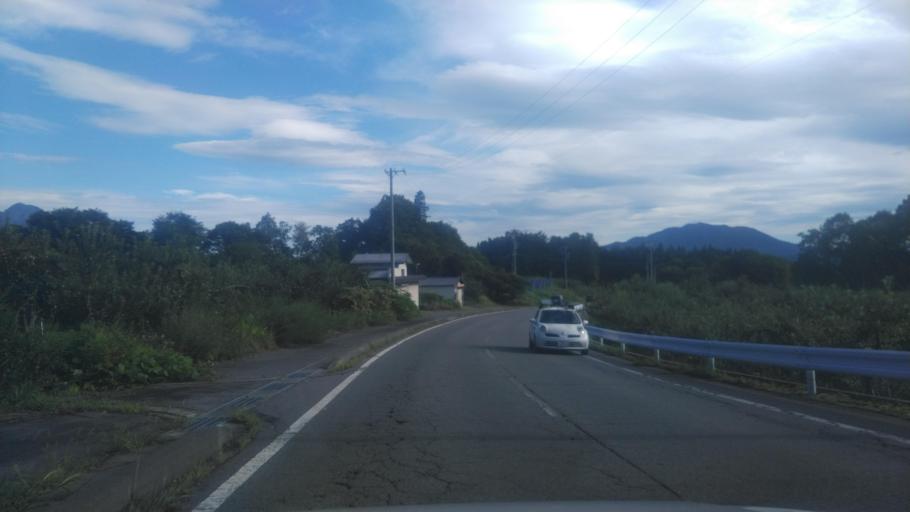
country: JP
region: Nagano
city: Nagano-shi
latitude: 36.7241
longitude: 138.2088
